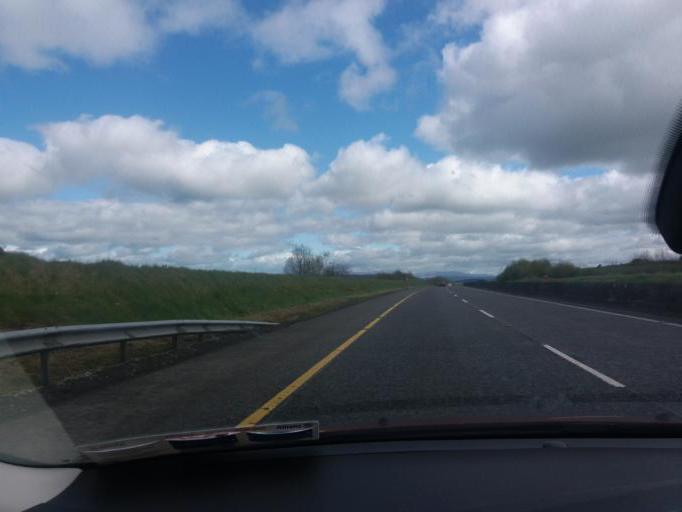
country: IE
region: Munster
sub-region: County Cork
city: Watergrasshill
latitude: 52.0397
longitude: -8.3159
